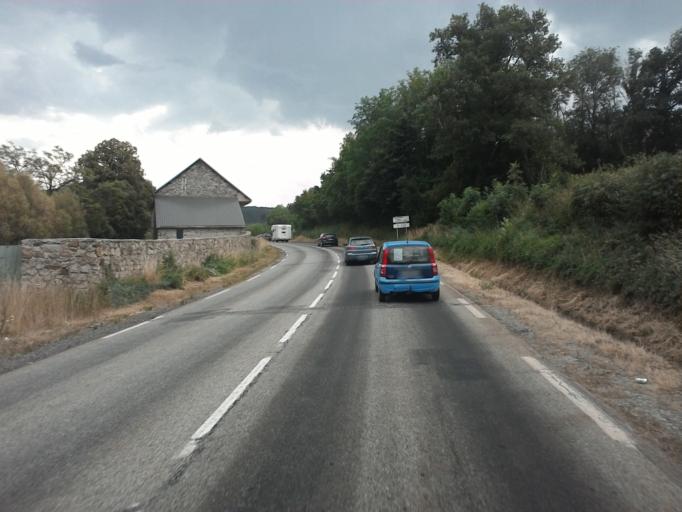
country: FR
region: Rhone-Alpes
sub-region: Departement de l'Isere
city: La Mure
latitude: 44.8928
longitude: 5.8232
